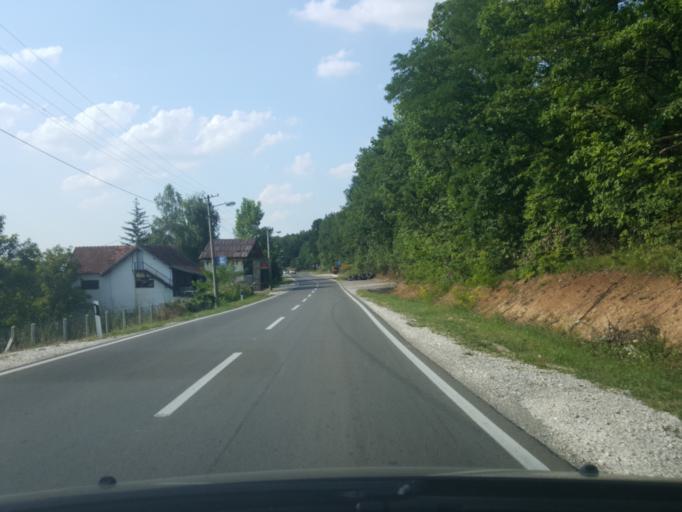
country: RS
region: Central Serbia
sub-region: Sumadijski Okrug
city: Topola
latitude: 44.2380
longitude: 20.6778
